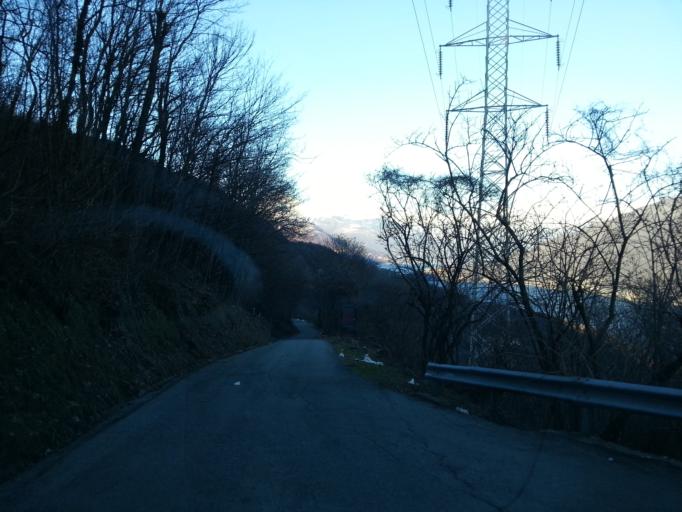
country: IT
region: Lombardy
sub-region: Provincia di Como
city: San Siro
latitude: 46.0642
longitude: 9.2565
